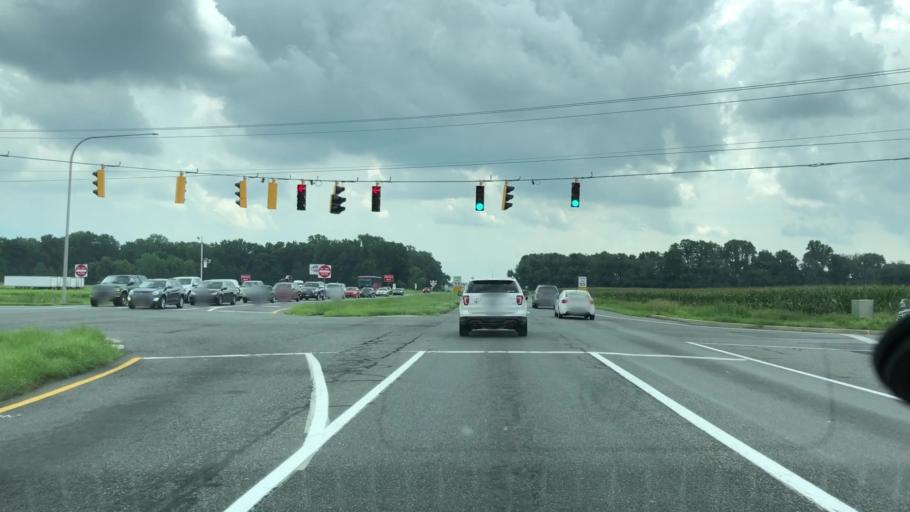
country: US
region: Delaware
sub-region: Sussex County
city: Bridgeville
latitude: 38.7495
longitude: -75.5934
